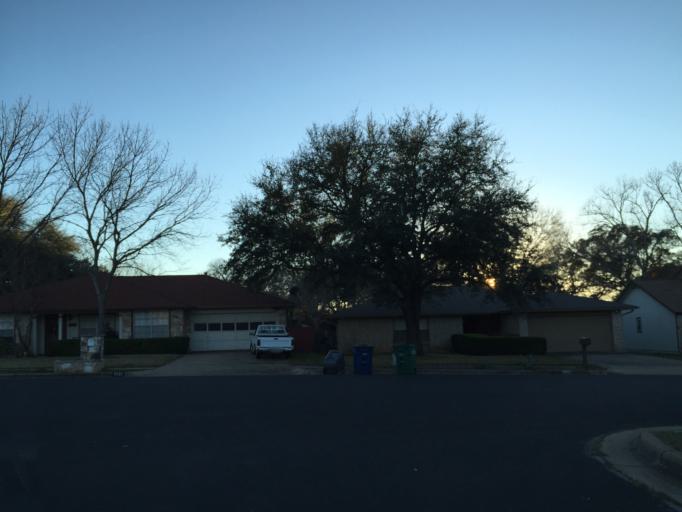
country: US
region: Texas
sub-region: Williamson County
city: Jollyville
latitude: 30.4288
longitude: -97.7787
